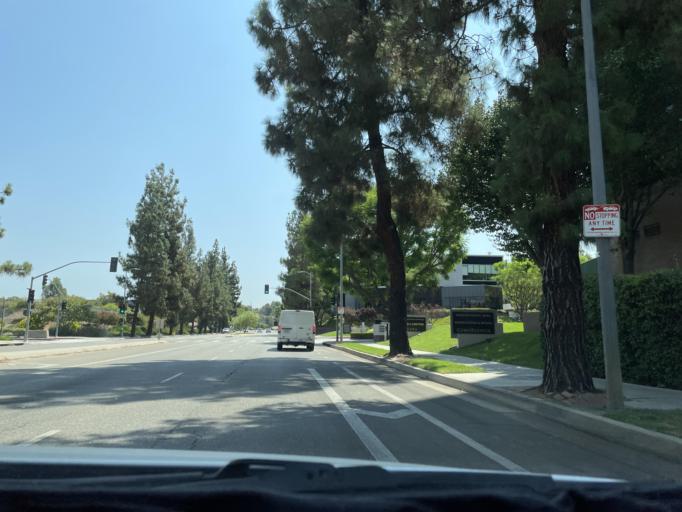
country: US
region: California
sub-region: Los Angeles County
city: Woodland Hills
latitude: 34.1792
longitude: -118.6002
